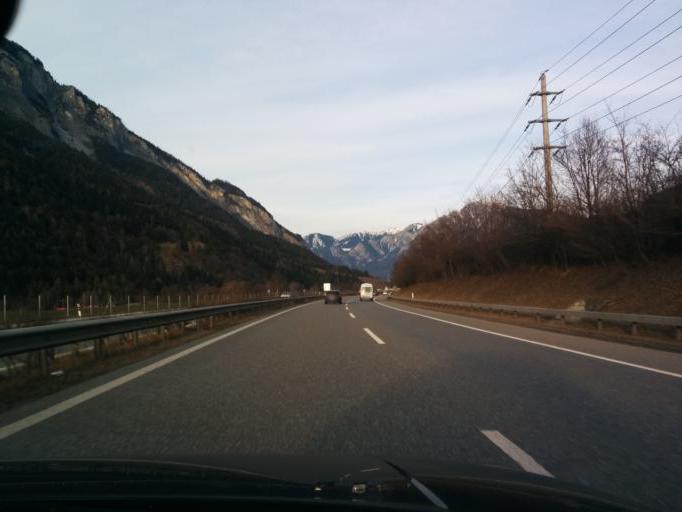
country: CH
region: Grisons
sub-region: Imboden District
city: Domat
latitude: 46.8348
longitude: 9.4379
